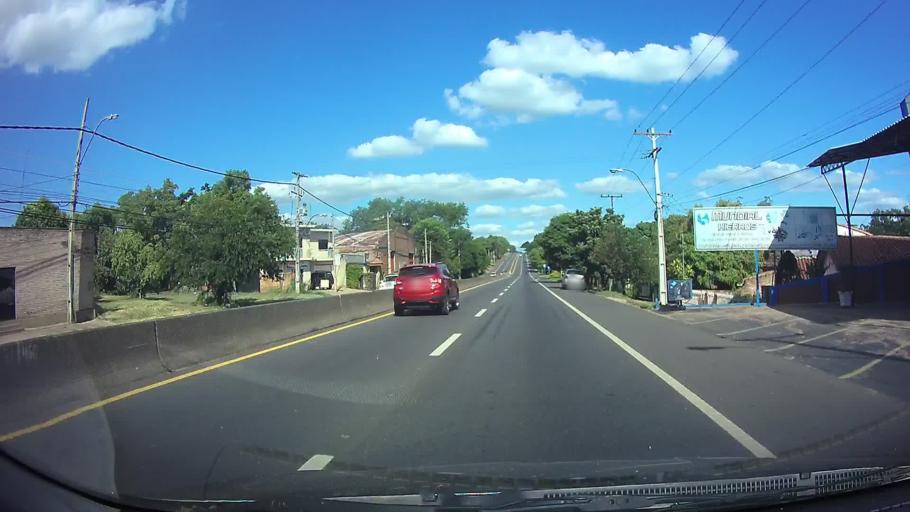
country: PY
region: Central
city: Itaugua
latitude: -25.3971
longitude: -57.3406
